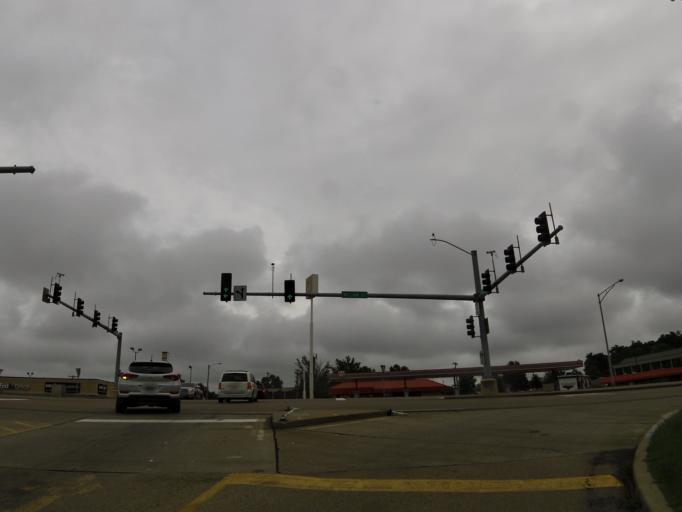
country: US
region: Missouri
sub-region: Cape Girardeau County
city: Cape Girardeau
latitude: 37.3023
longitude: -89.5770
